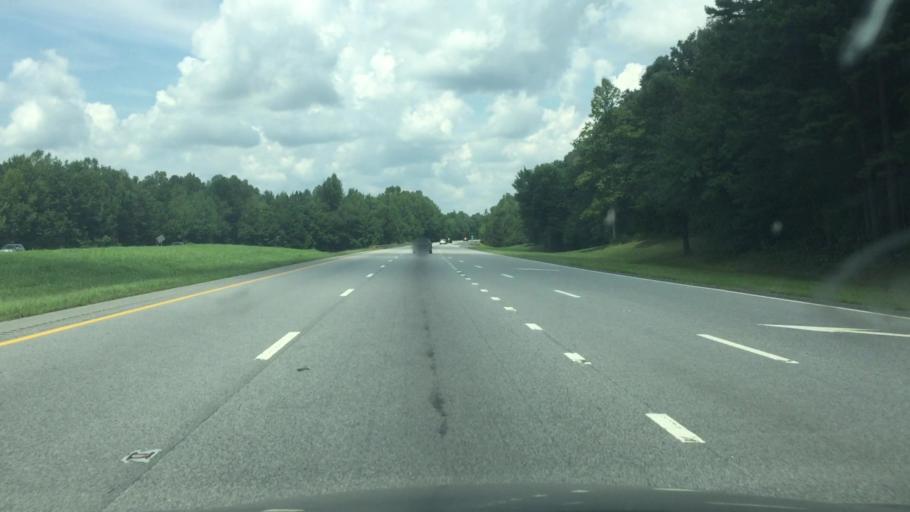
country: US
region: North Carolina
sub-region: Guilford County
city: Pleasant Garden
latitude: 35.9270
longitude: -79.8267
